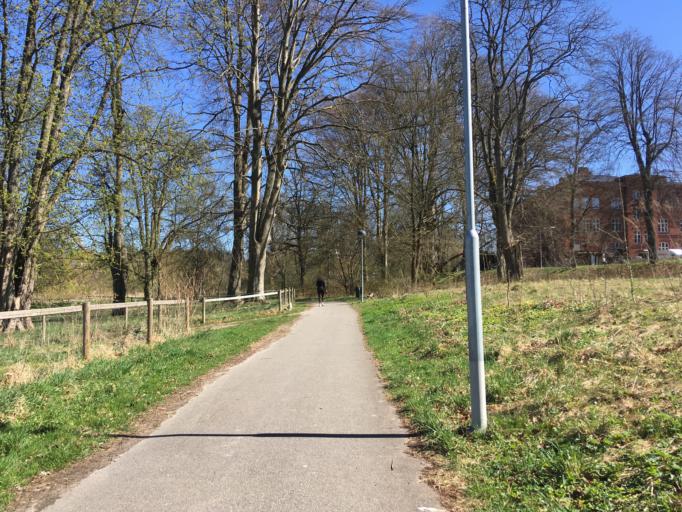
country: SE
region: Skane
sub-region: Lunds Kommun
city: Lund
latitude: 55.6850
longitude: 13.1751
